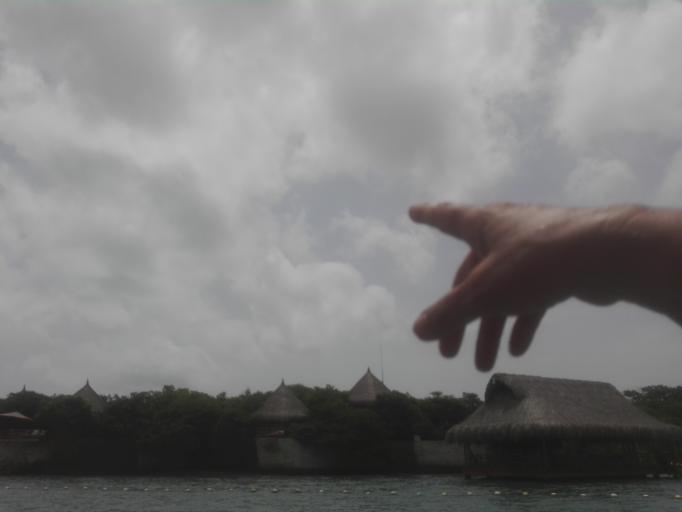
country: CO
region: Bolivar
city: Turbana
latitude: 10.1540
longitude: -75.6866
